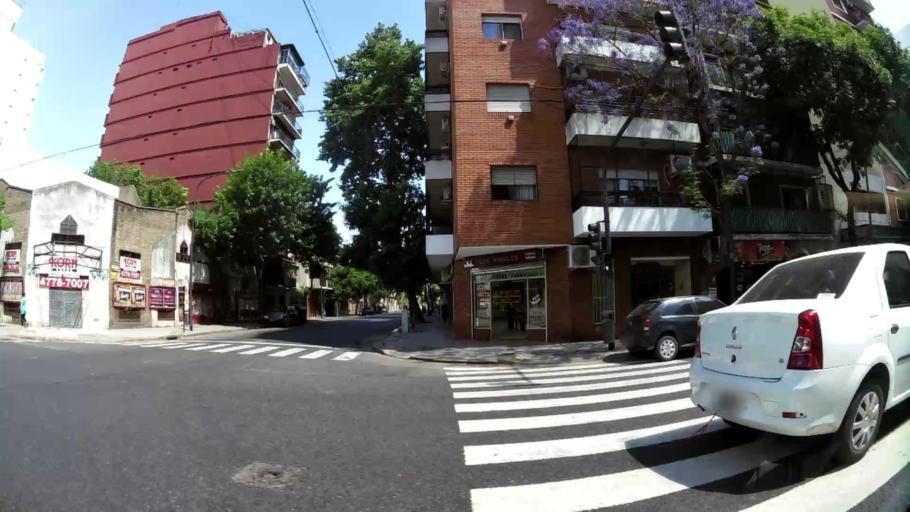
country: AR
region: Buenos Aires F.D.
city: Buenos Aires
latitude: -34.6187
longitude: -58.4012
